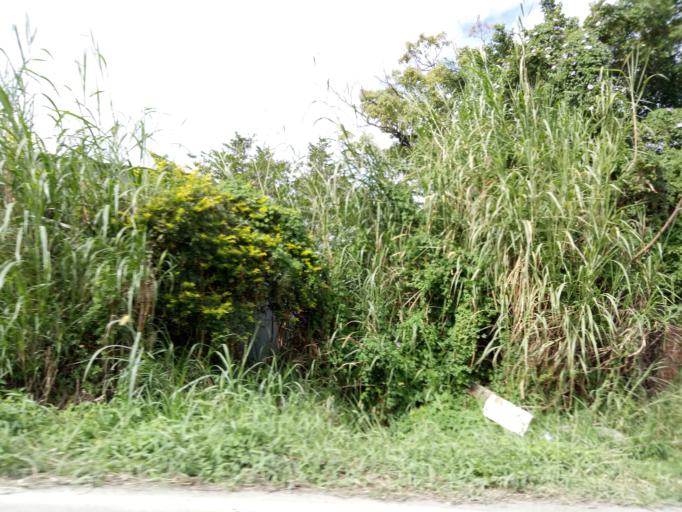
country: TW
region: Taiwan
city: Daxi
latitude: 24.8984
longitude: 121.2896
